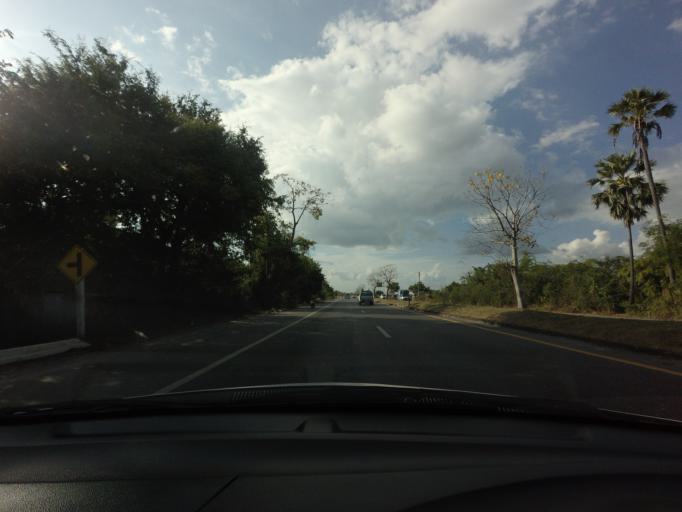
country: TH
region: Nakhon Nayok
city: Nakhon Nayok
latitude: 14.2233
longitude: 101.1990
